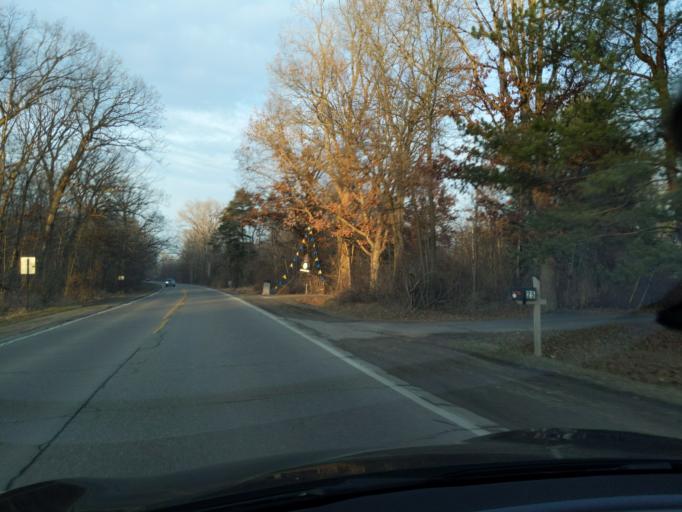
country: US
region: Michigan
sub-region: Livingston County
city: Brighton
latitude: 42.6031
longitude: -83.7493
